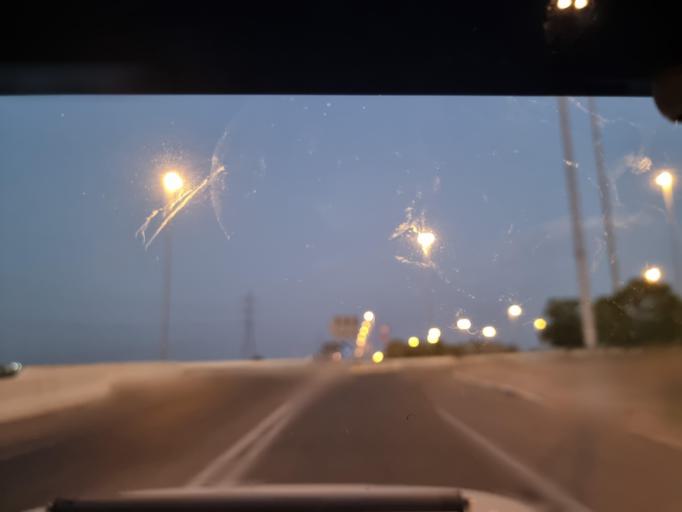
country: AE
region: Abu Dhabi
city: Abu Dhabi
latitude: 24.1916
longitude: 55.0024
